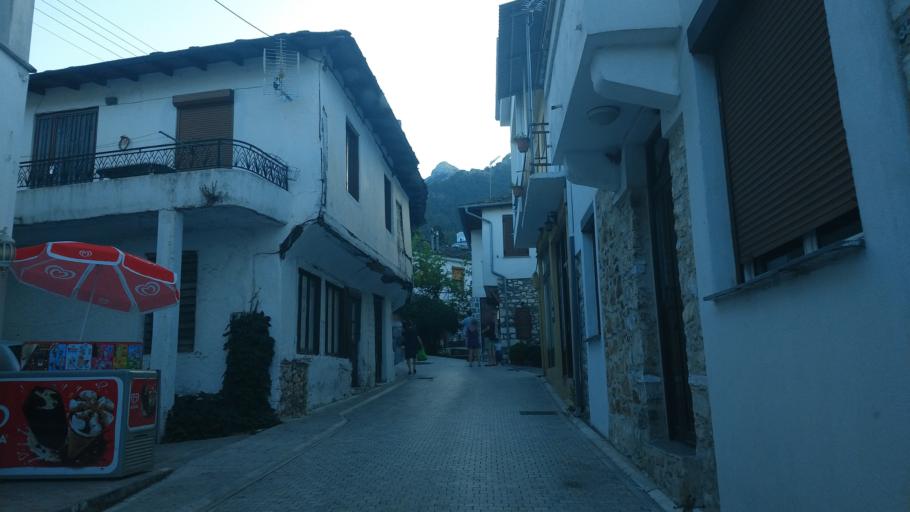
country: GR
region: East Macedonia and Thrace
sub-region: Nomos Kavalas
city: Potamia
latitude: 40.7312
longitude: 24.7285
